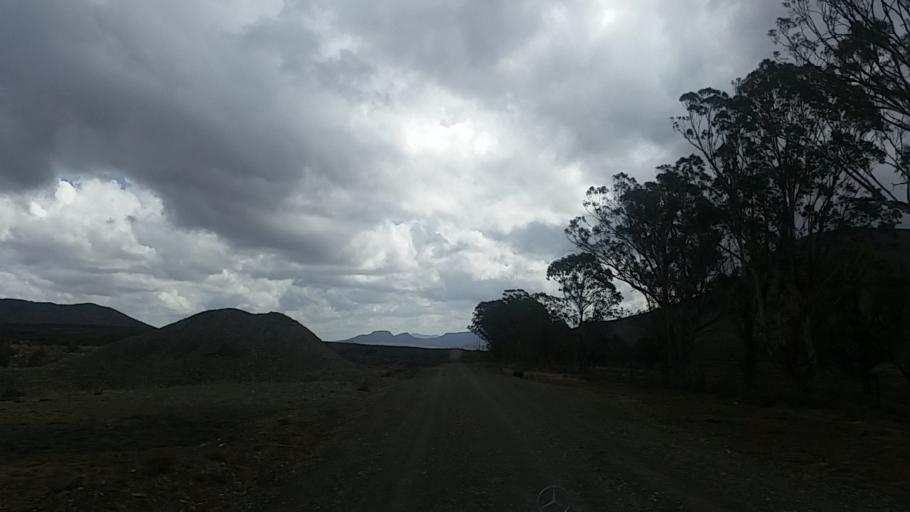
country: ZA
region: Eastern Cape
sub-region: Chris Hani District Municipality
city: Middelburg
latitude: -31.7894
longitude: 24.6739
